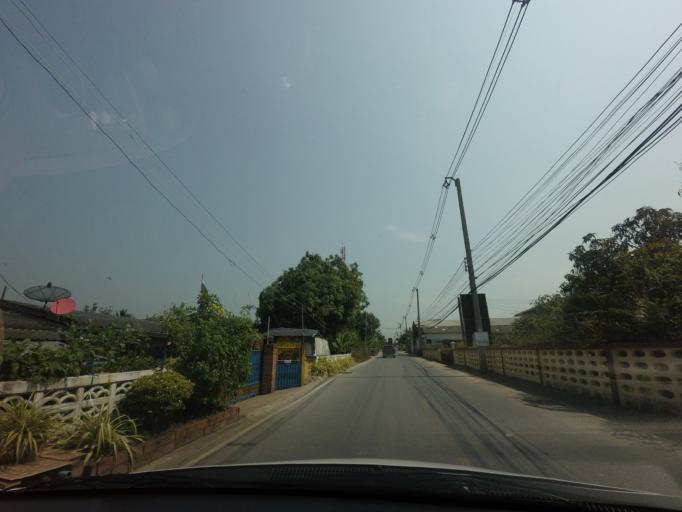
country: TH
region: Nakhon Pathom
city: Sam Phran
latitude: 13.7588
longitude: 100.2474
